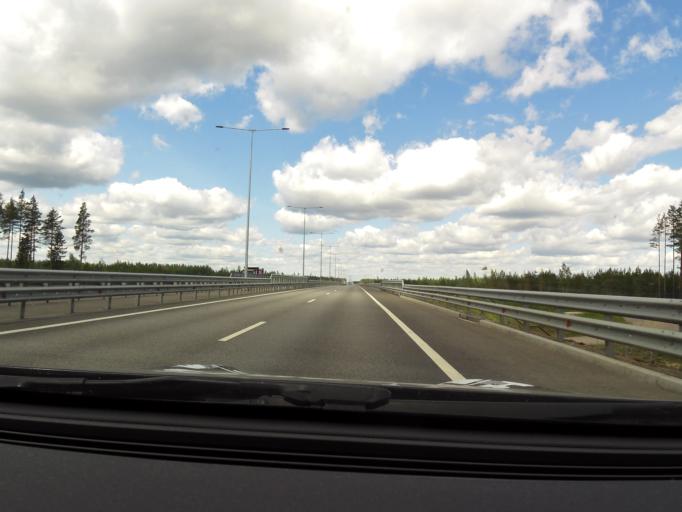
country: RU
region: Tverskaya
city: Vyshniy Volochek
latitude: 57.4340
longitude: 34.4625
